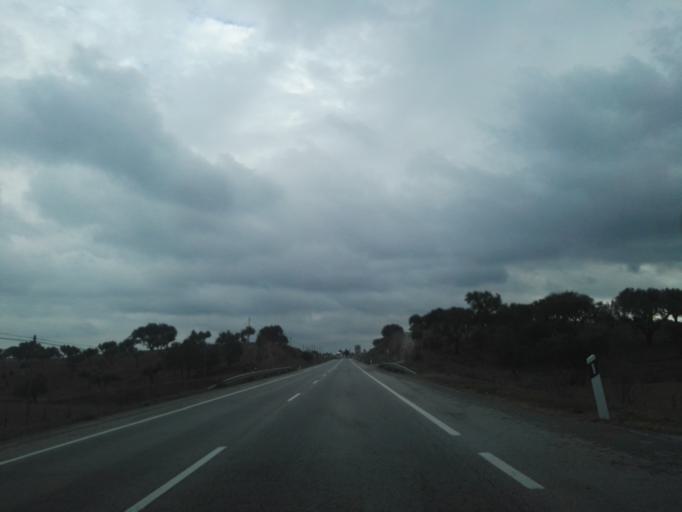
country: PT
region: Portalegre
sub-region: Arronches
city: Arronches
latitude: 39.1379
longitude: -7.2951
